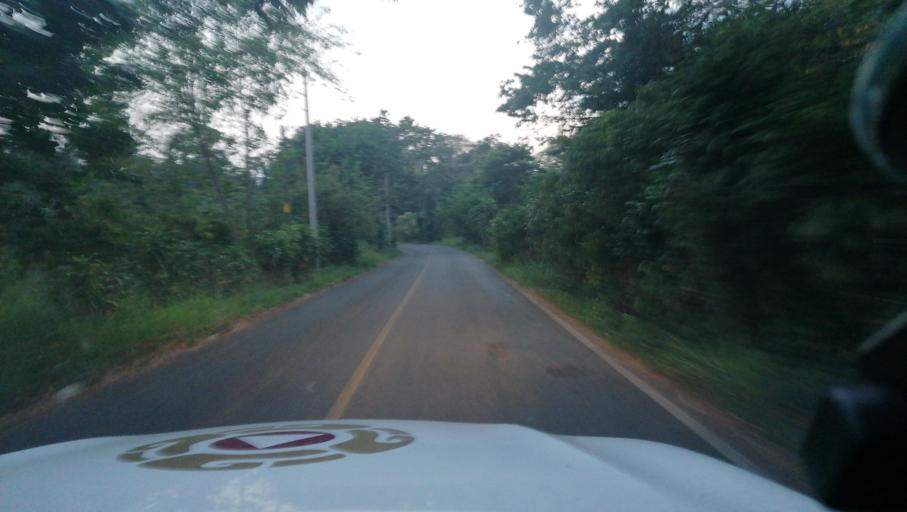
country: MX
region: Chiapas
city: Veinte de Noviembre
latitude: 15.0112
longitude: -92.2459
